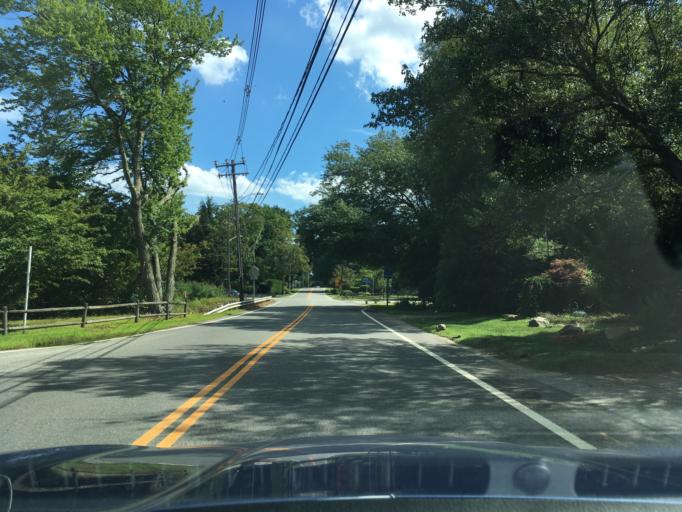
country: US
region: Rhode Island
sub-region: Bristol County
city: Barrington
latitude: 41.7398
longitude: -71.3307
